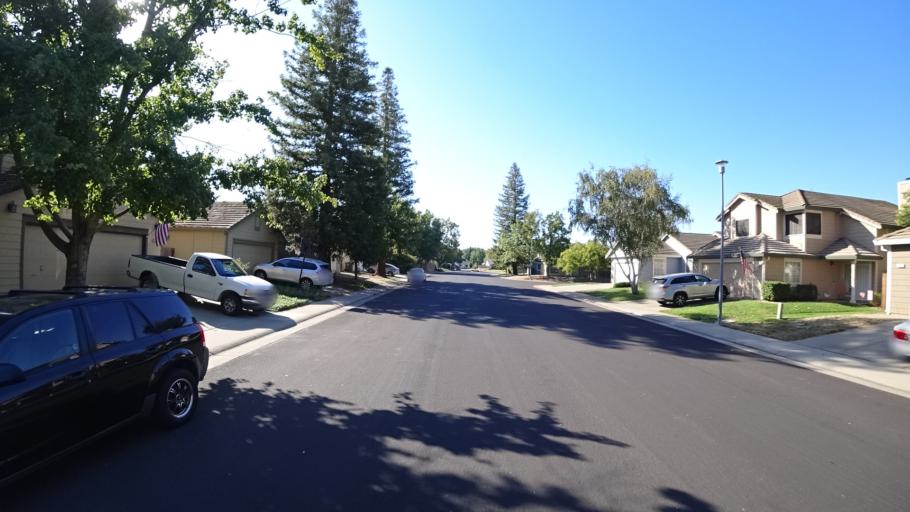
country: US
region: California
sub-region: Sacramento County
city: Laguna
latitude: 38.4315
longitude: -121.4417
